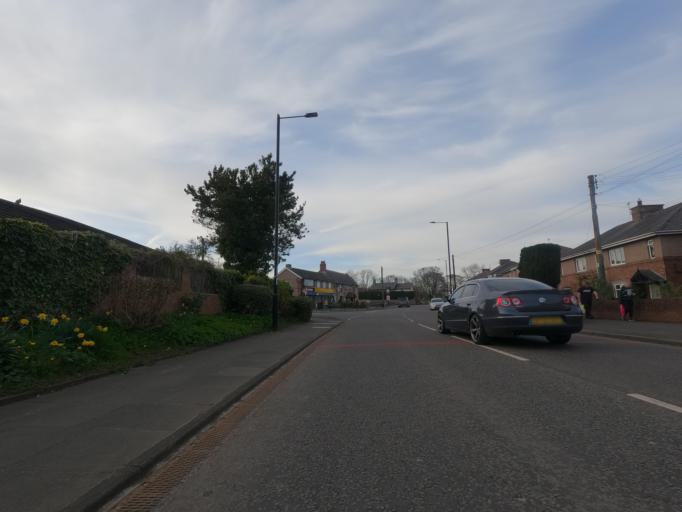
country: GB
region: England
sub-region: Newcastle upon Tyne
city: Dinnington
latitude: 55.0537
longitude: -1.6751
